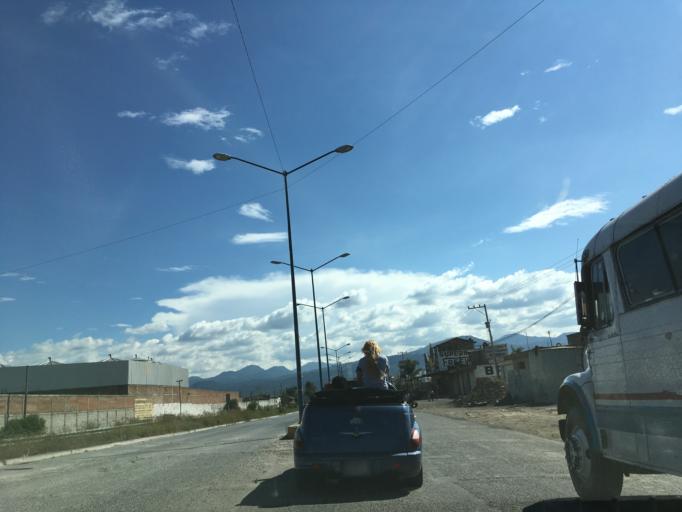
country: MX
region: Michoacan
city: Zacapu
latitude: 19.8391
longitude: -101.7681
